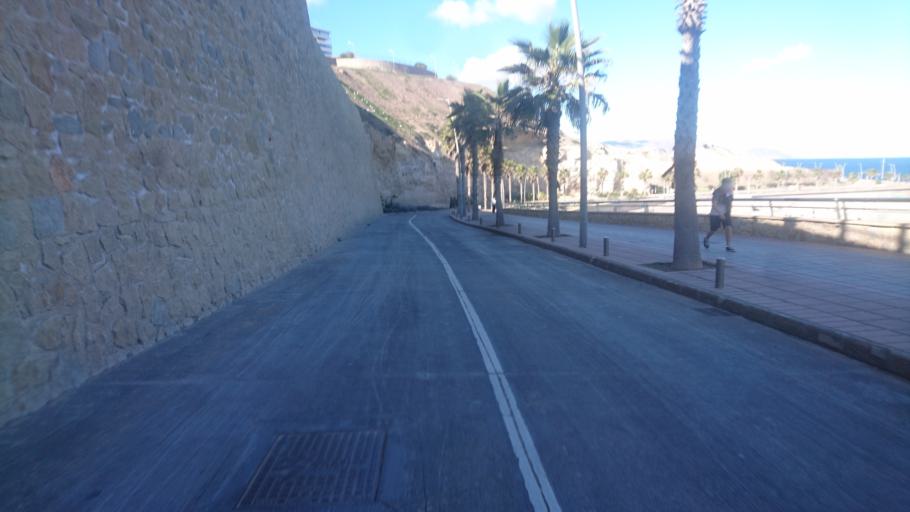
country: ES
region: Melilla
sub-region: Melilla
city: Melilla
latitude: 35.2973
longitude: -2.9360
